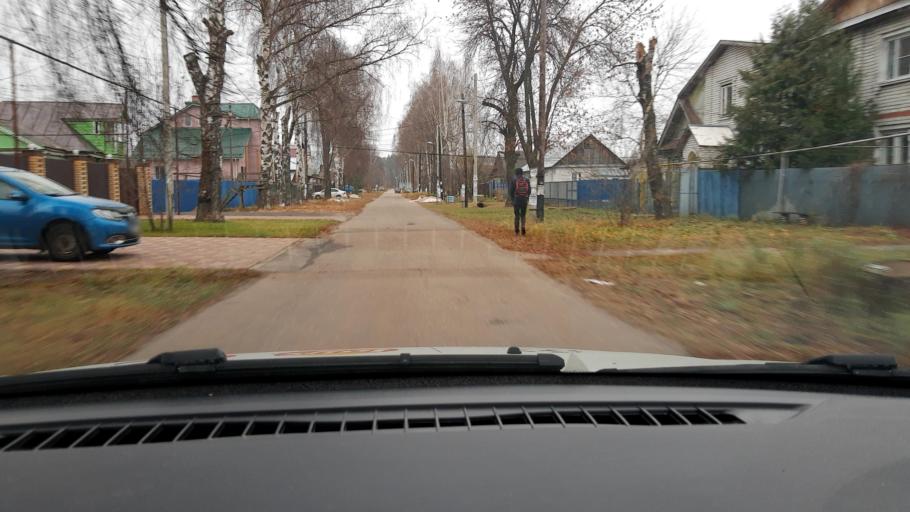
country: RU
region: Nizjnij Novgorod
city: Gorbatovka
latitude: 56.2023
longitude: 43.7698
